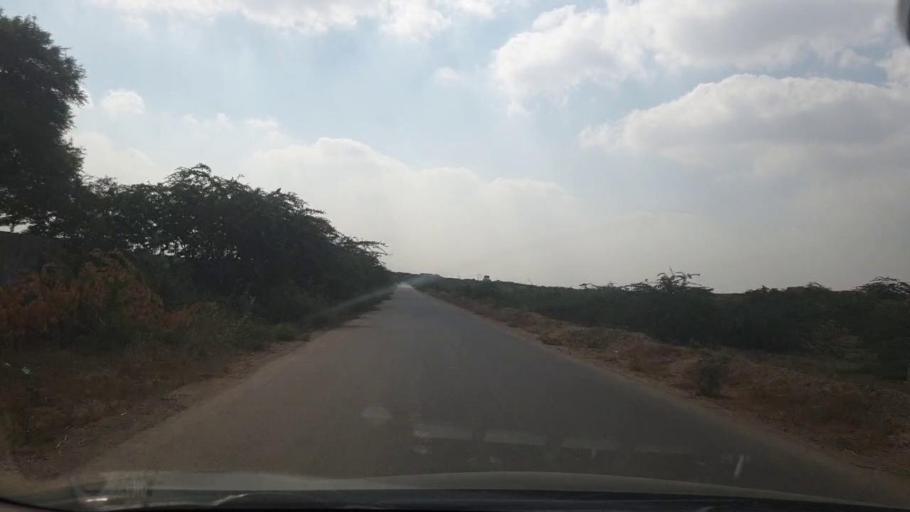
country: PK
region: Sindh
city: Malir Cantonment
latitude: 25.0194
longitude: 67.3543
